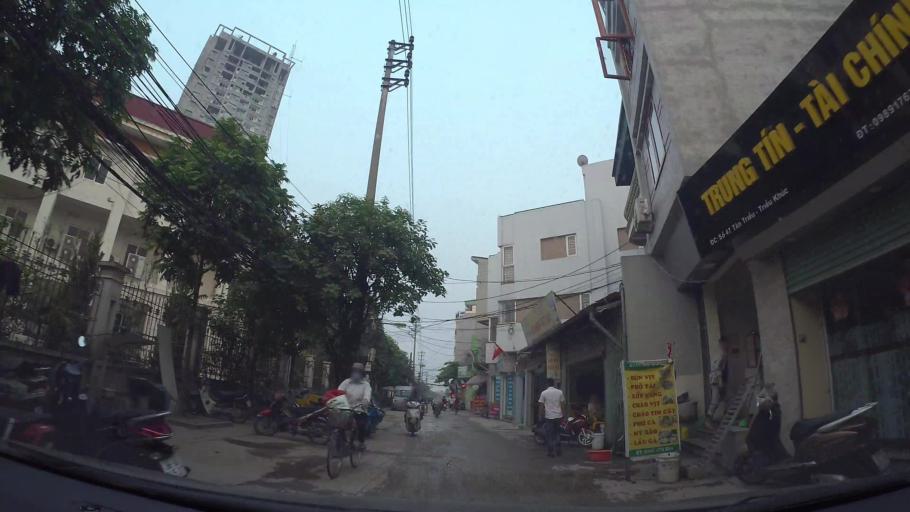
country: VN
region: Ha Noi
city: Thanh Xuan
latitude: 20.9799
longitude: 105.8056
